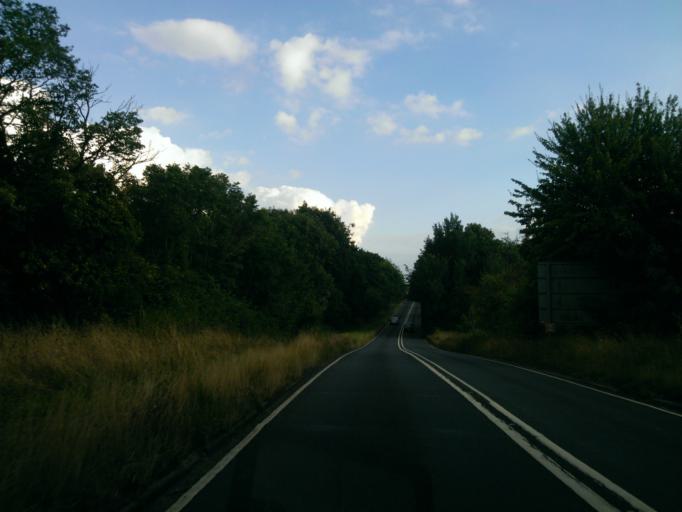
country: GB
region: England
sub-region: Essex
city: Sible Hedingham
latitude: 51.9878
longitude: 0.5860
